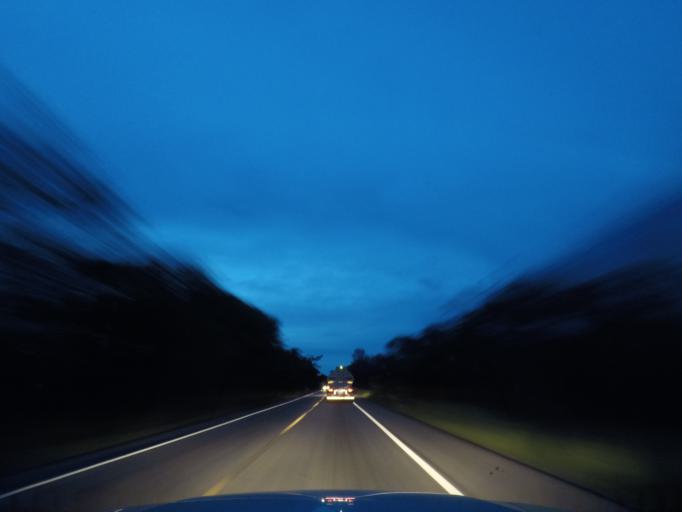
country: BR
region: Bahia
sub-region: Andarai
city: Vera Cruz
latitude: -12.4943
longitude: -41.3353
